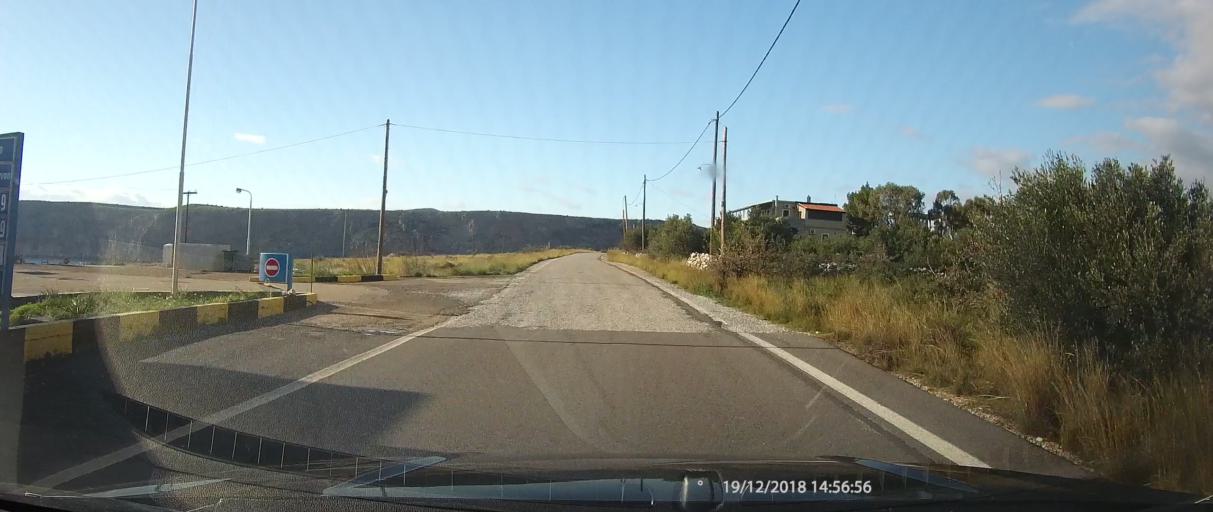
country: GR
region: Peloponnese
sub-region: Nomos Lakonias
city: Gytheio
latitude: 36.4790
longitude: 22.4118
